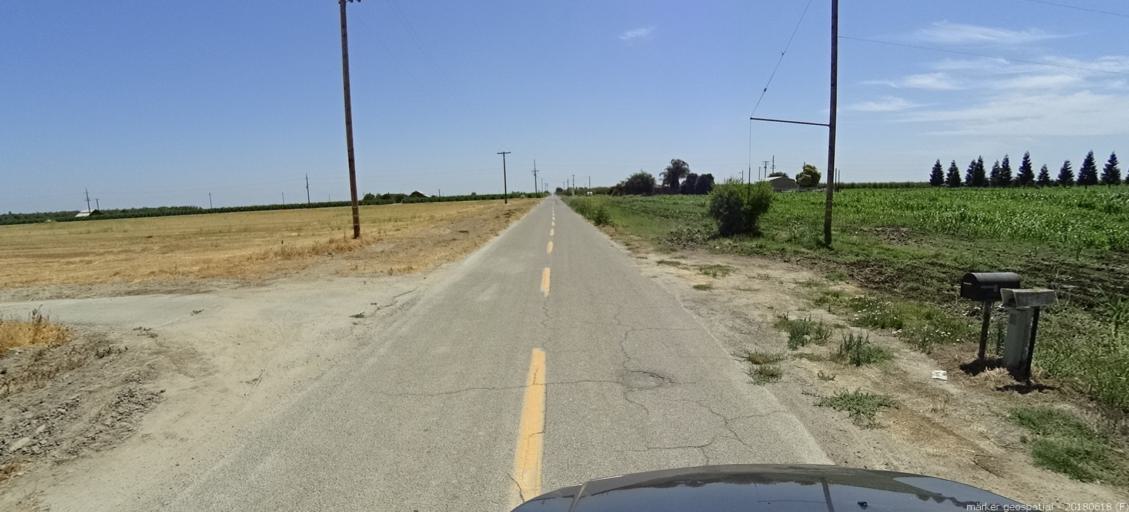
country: US
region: California
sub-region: Madera County
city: Parkwood
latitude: 36.8585
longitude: -120.1127
